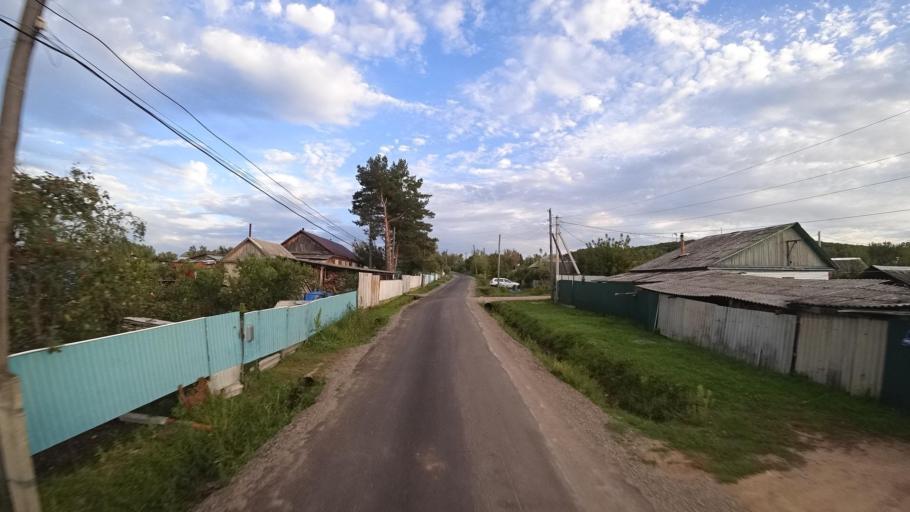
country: RU
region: Primorskiy
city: Yakovlevka
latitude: 44.4232
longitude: 133.4660
